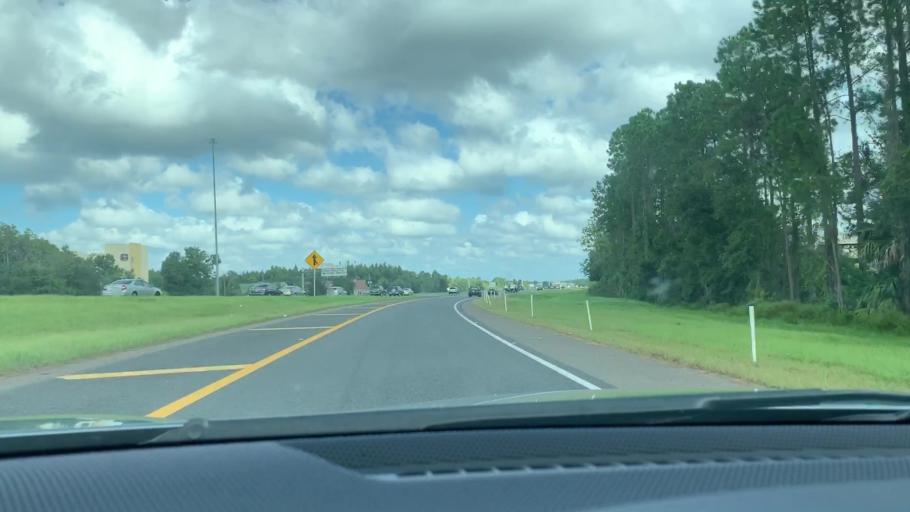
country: US
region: Florida
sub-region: Hillsborough County
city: Pebble Creek
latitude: 28.1259
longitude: -82.3751
